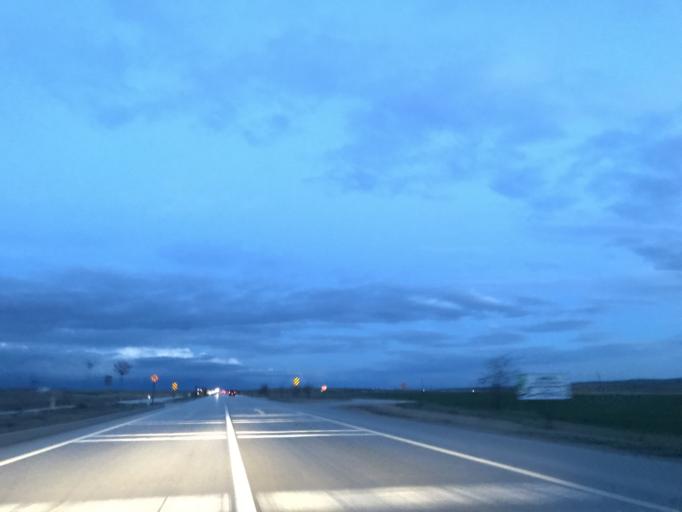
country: TR
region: Konya
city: Kulu
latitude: 39.1716
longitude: 33.1566
